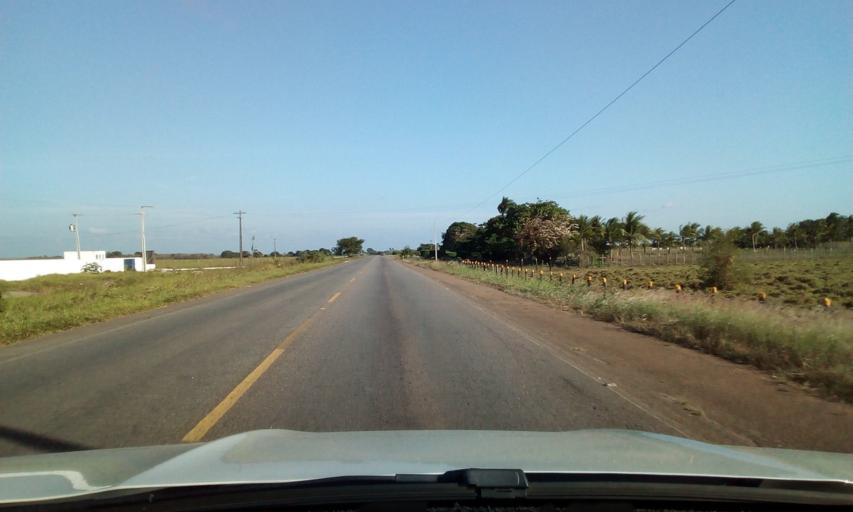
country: BR
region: Paraiba
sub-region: Mari
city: Mari
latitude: -7.0171
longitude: -35.3537
